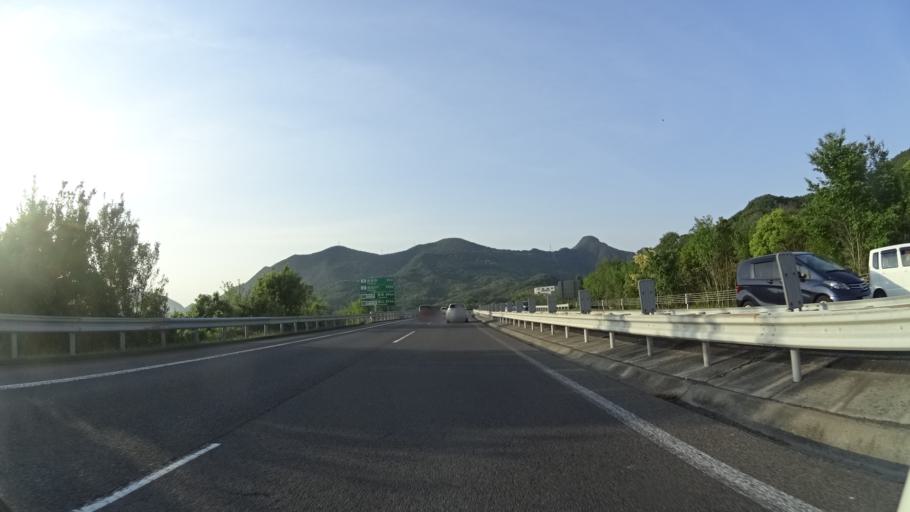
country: JP
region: Kagawa
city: Tadotsu
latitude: 34.2137
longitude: 133.7285
